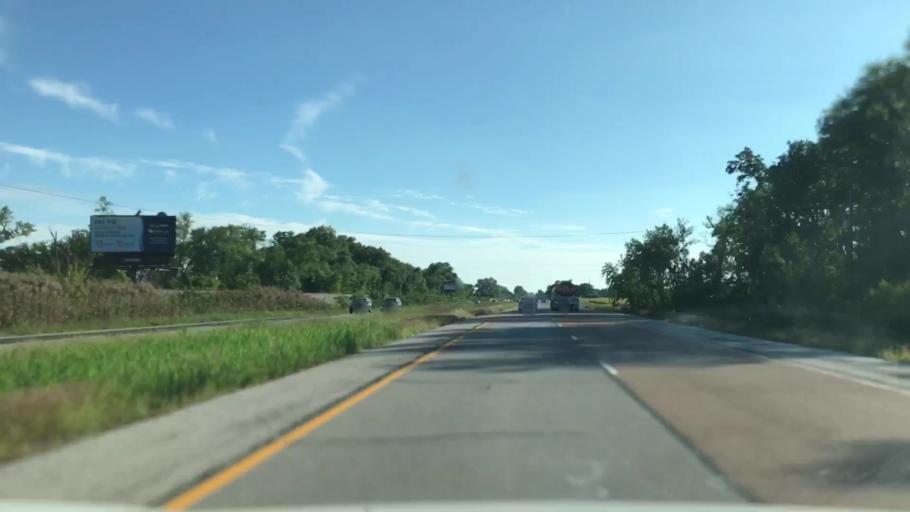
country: US
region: Illinois
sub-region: Madison County
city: Mitchell
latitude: 38.7948
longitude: -90.1028
